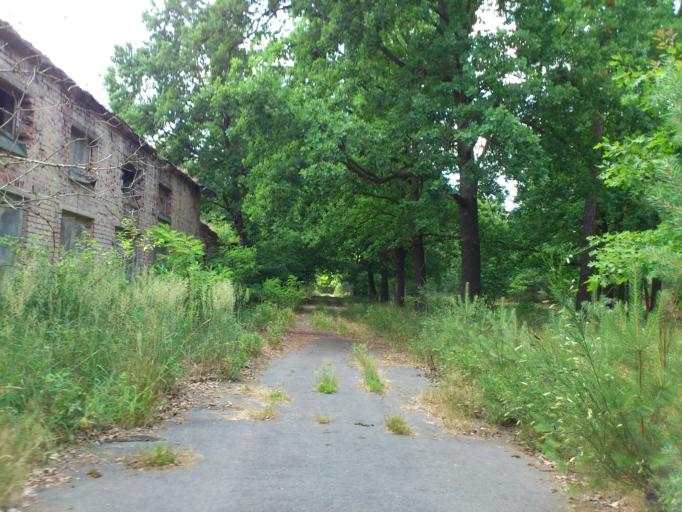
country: DE
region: Saxony
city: Konigsbruck
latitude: 51.2791
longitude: 13.8860
